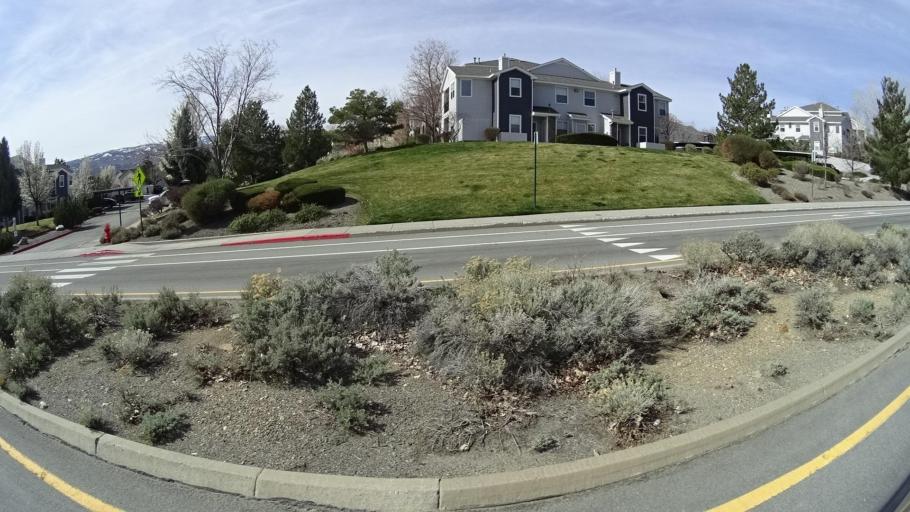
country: US
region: Nevada
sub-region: Washoe County
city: Mogul
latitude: 39.5406
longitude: -119.8881
